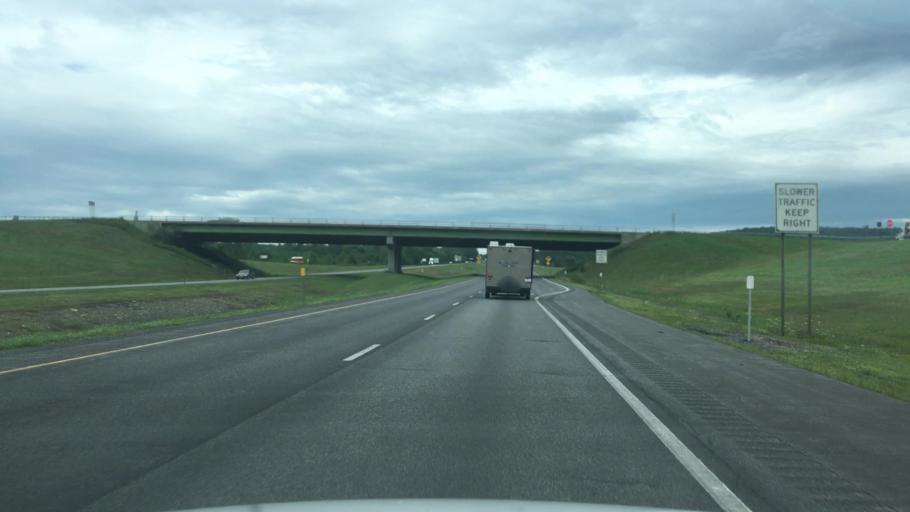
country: US
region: New York
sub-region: Schoharie County
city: Schoharie
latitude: 42.7066
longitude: -74.3157
